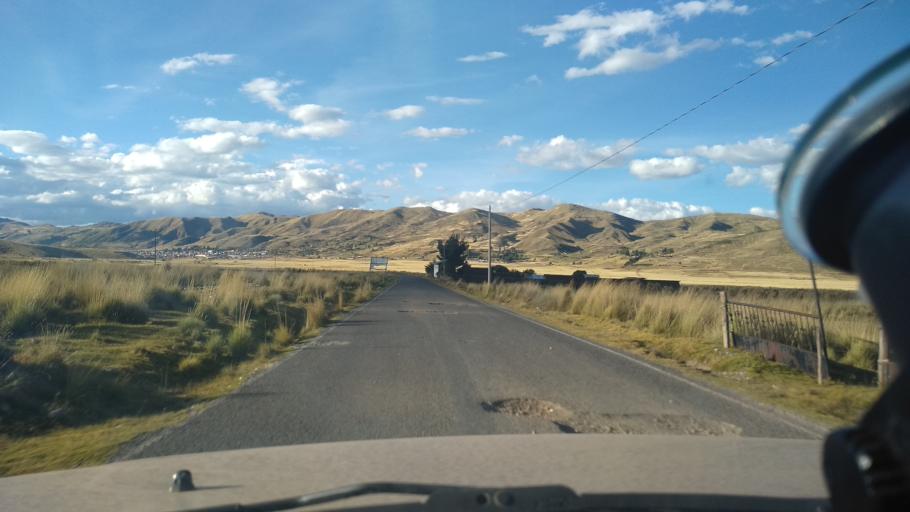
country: PE
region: Cusco
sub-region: Provincia de Canas
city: Chignayhua
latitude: -14.2504
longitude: -71.4362
